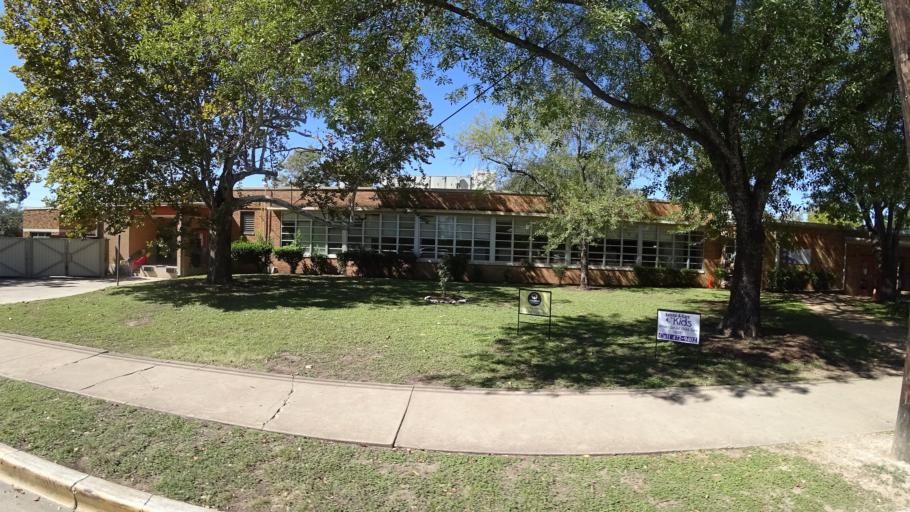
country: US
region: Texas
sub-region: Travis County
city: Austin
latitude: 30.2931
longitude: -97.7140
